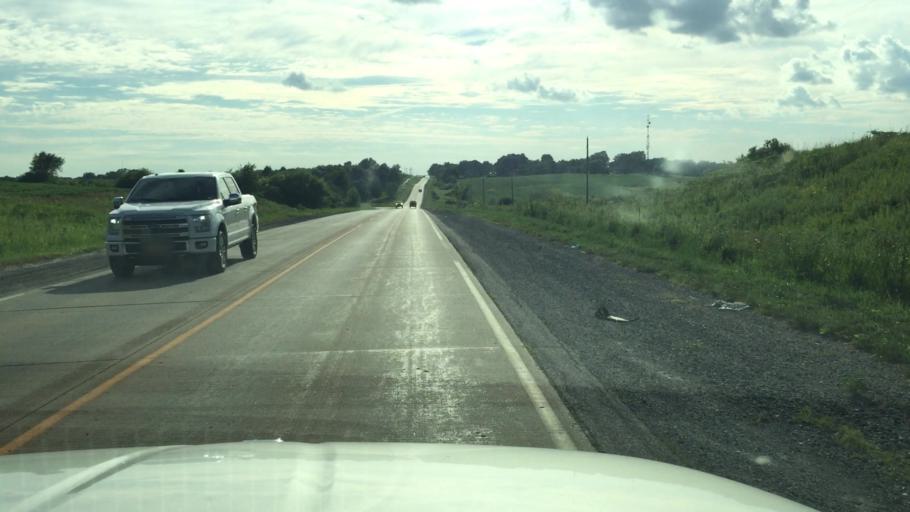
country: US
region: Iowa
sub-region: Johnson County
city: Iowa City
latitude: 41.6710
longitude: -91.4593
